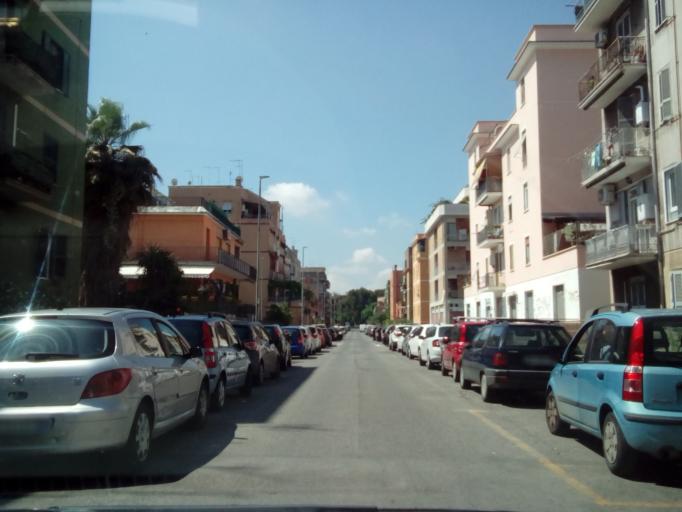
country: IT
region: Latium
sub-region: Citta metropolitana di Roma Capitale
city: Rome
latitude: 41.8770
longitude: 12.5708
